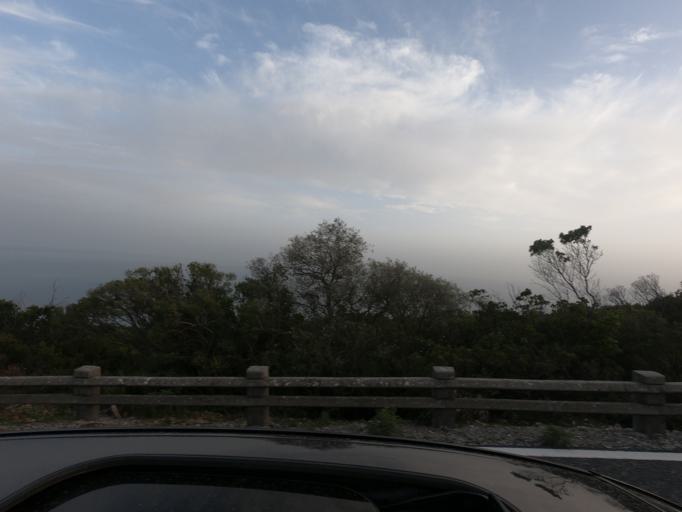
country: PT
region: Setubal
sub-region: Setubal
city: Setubal
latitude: 38.4887
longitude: -8.9477
